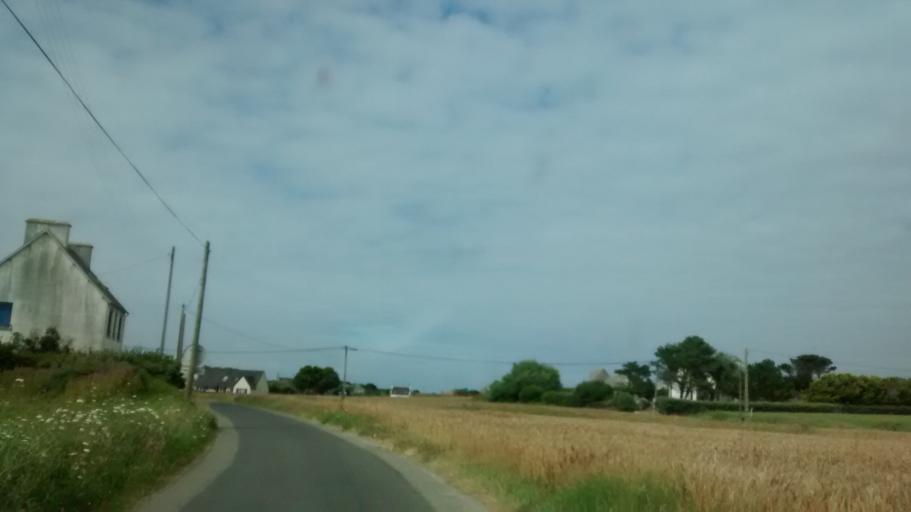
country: FR
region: Brittany
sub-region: Departement du Finistere
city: Plouneour-Trez
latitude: 48.6705
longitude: -4.3419
